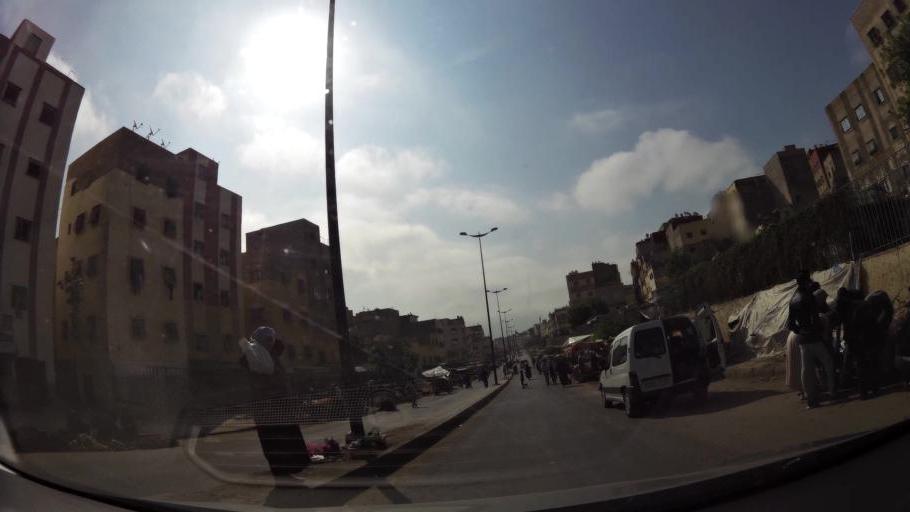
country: MA
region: Fes-Boulemane
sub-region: Fes
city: Fes
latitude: 34.0691
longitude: -5.0089
